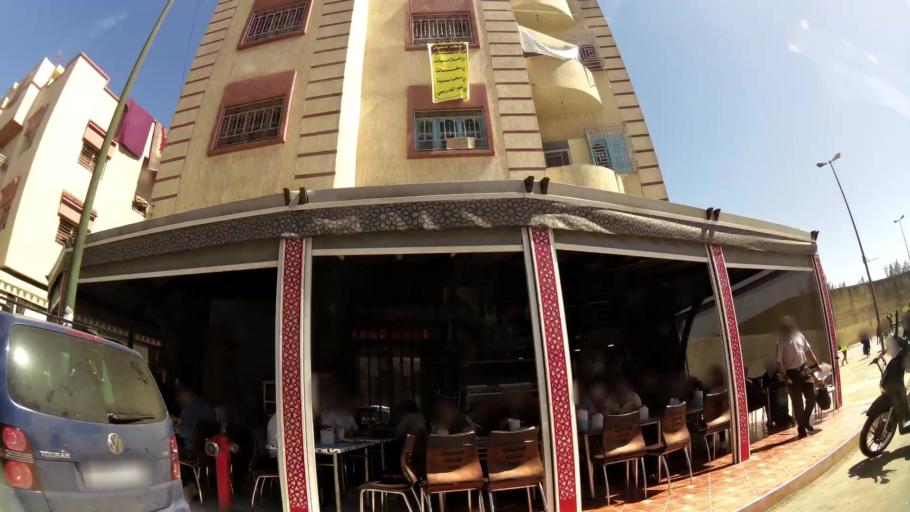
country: MA
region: Meknes-Tafilalet
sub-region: Meknes
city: Meknes
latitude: 33.8664
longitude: -5.5527
